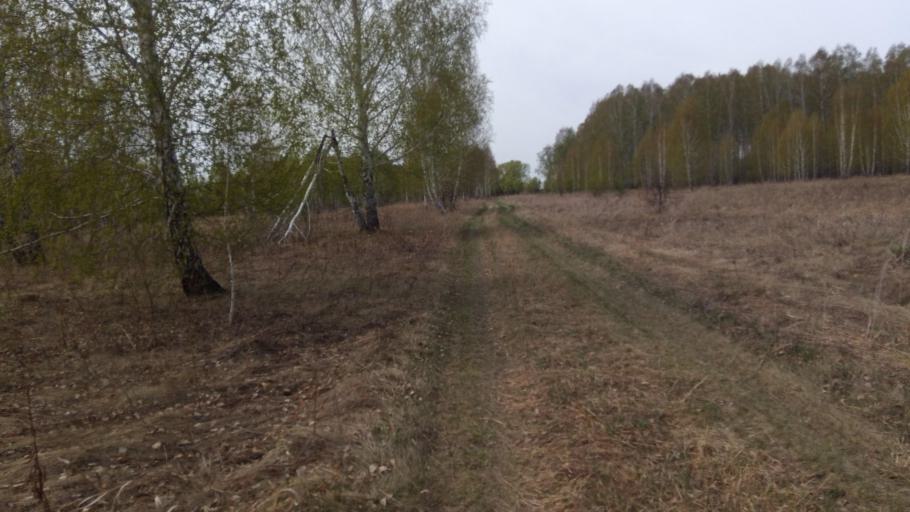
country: RU
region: Chelyabinsk
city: Timiryazevskiy
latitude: 55.0033
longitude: 60.8522
